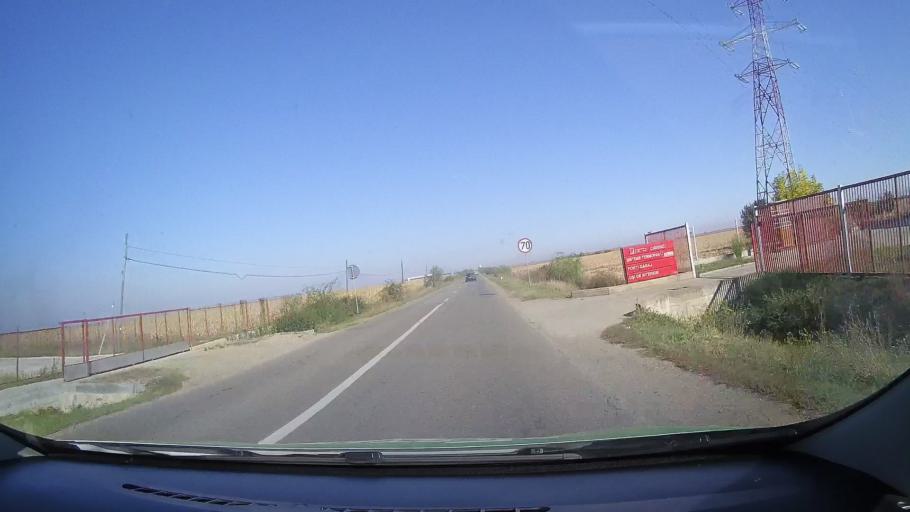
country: RO
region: Satu Mare
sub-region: Oras Tasnad
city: Tasnad
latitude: 47.4964
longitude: 22.5753
